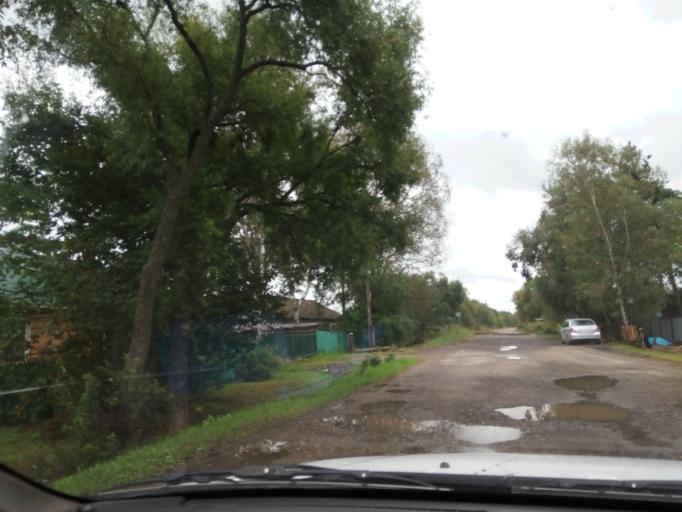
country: RU
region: Primorskiy
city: Dal'nerechensk
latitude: 45.9166
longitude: 133.7243
